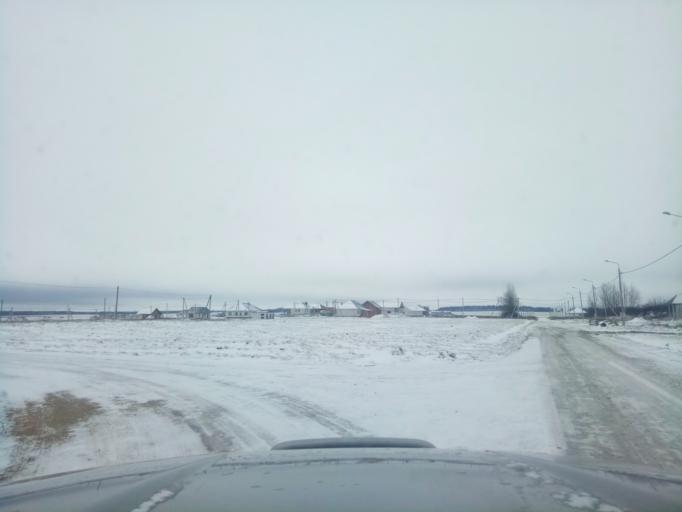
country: BY
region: Minsk
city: Kapyl'
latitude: 53.1622
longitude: 27.0813
